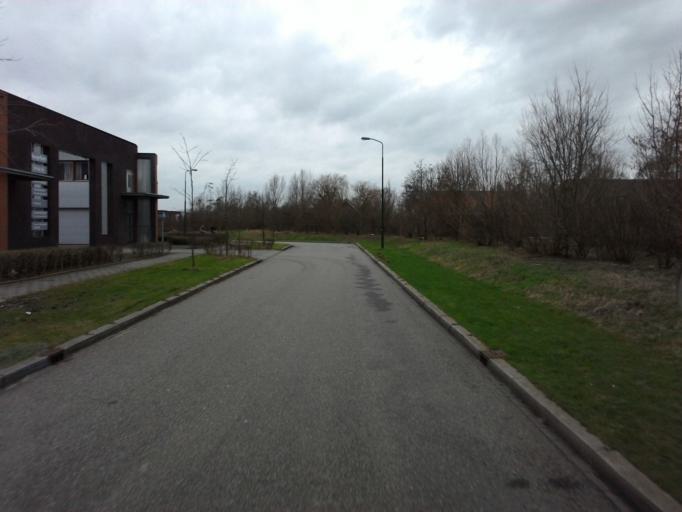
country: NL
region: Utrecht
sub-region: Gemeente Houten
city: Houten
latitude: 52.0228
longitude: 5.1530
